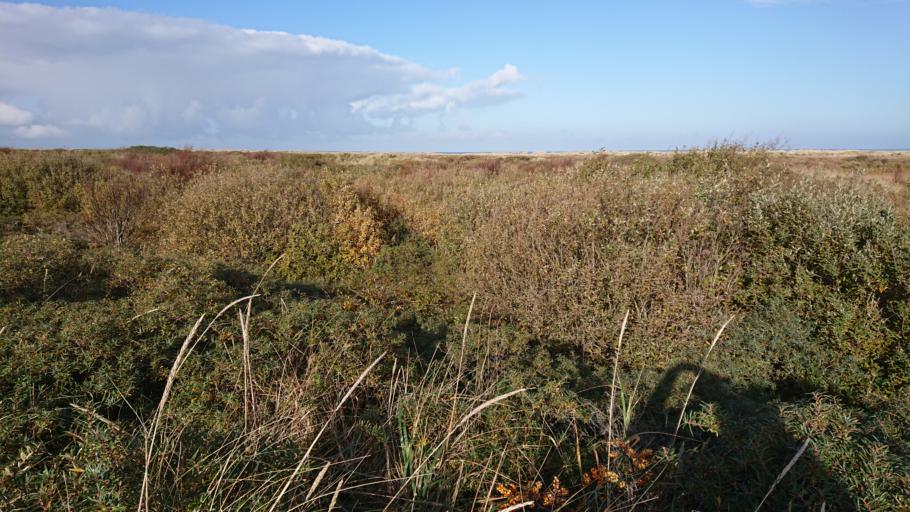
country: DK
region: North Denmark
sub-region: Frederikshavn Kommune
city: Skagen
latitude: 57.7457
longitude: 10.6323
